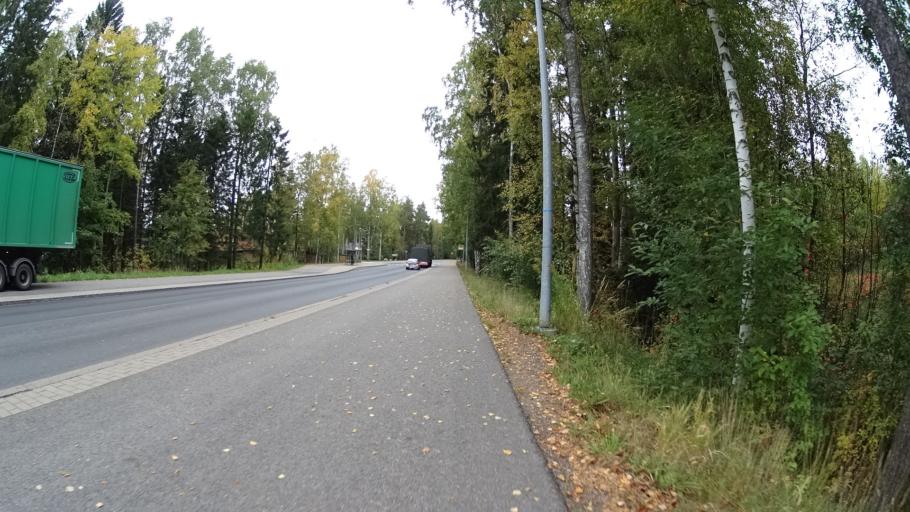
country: FI
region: Uusimaa
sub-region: Helsinki
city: Vantaa
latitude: 60.2195
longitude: 25.0577
